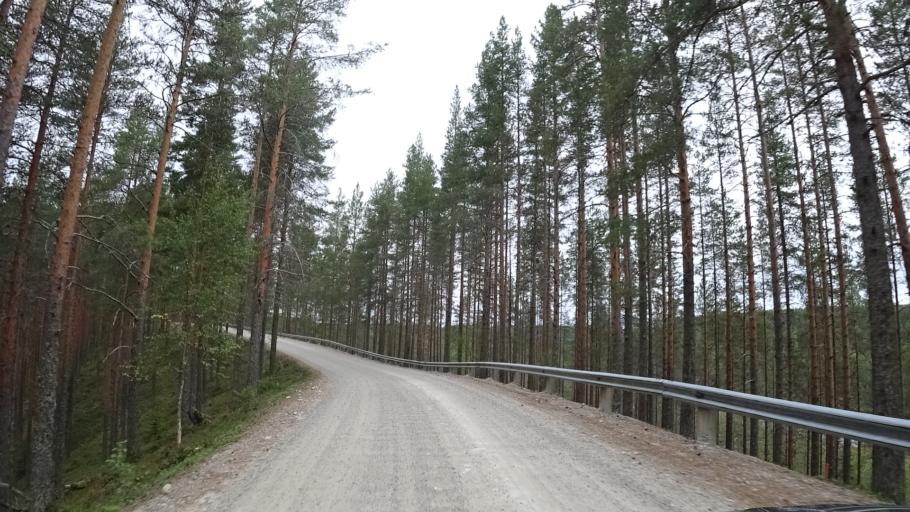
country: FI
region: North Karelia
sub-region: Pielisen Karjala
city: Lieksa
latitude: 63.2118
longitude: 30.4162
